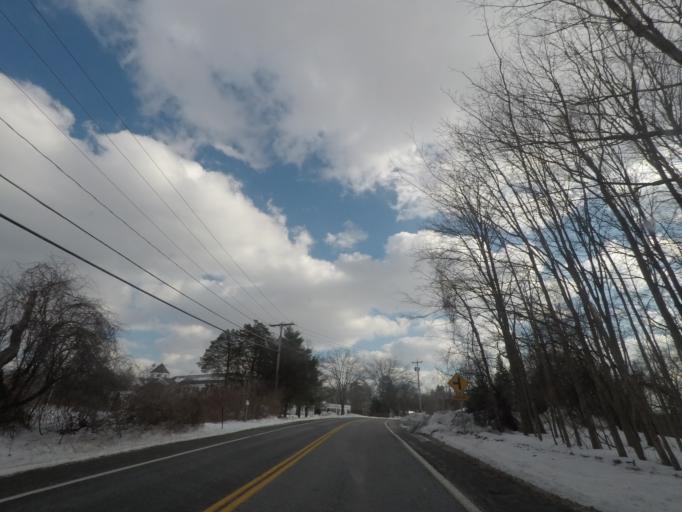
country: US
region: New York
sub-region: Schenectady County
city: East Glenville
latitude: 42.8553
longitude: -73.8843
